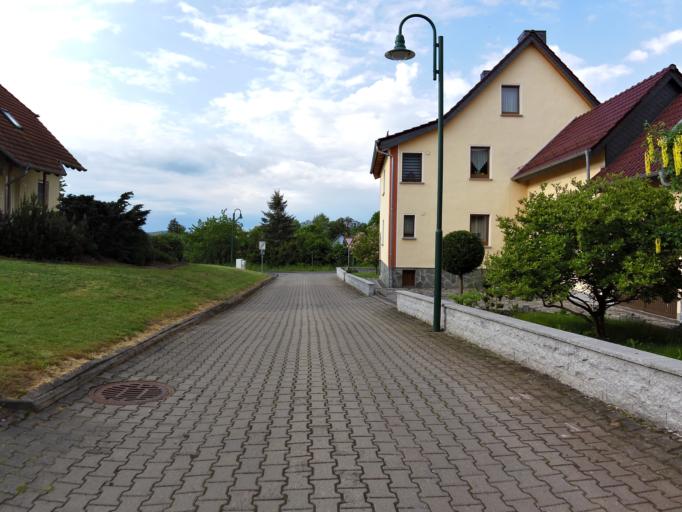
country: DE
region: Thuringia
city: Frauensee
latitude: 50.9054
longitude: 10.1056
